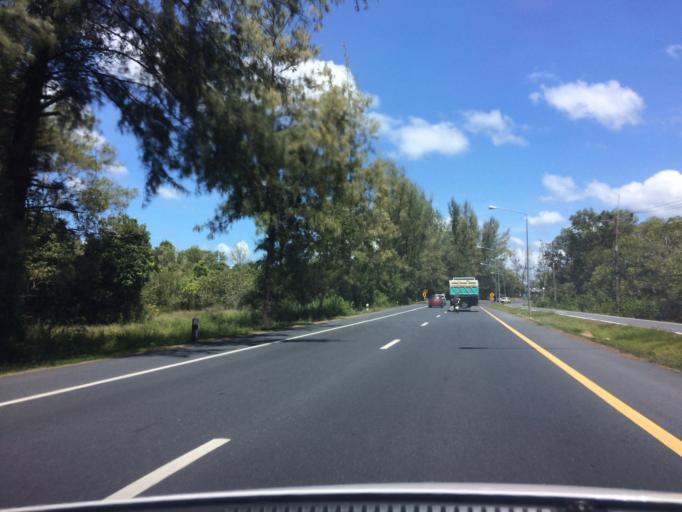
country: TH
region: Phuket
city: Thalang
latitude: 8.1934
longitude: 98.2897
